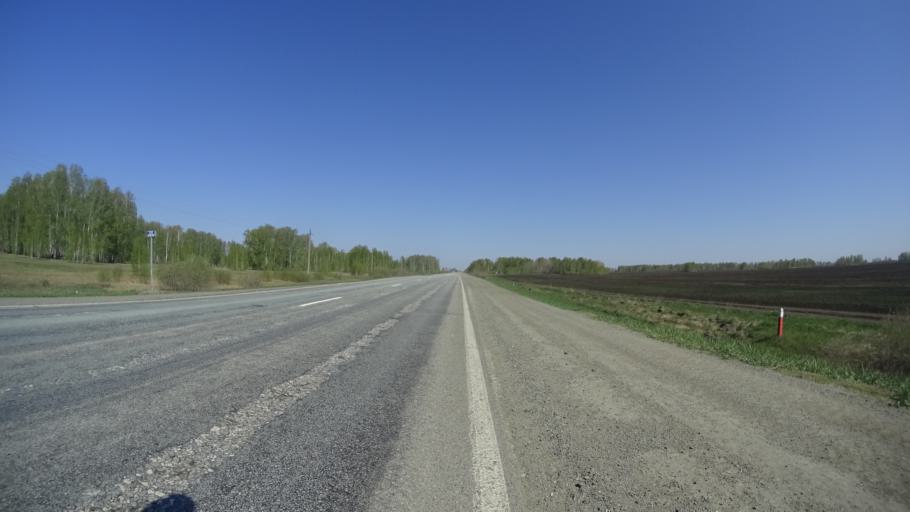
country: RU
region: Chelyabinsk
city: Troitsk
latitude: 54.1795
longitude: 61.4350
